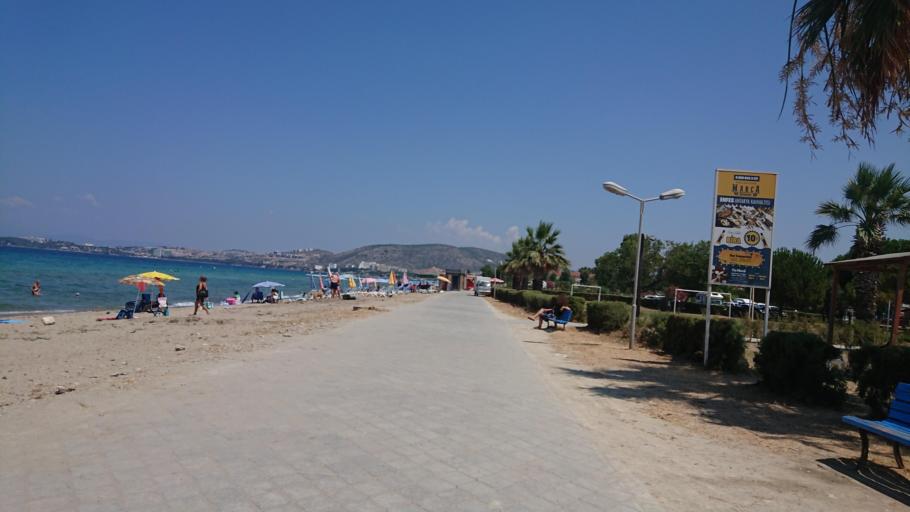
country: TR
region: Aydin
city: Kusadasi
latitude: 37.7964
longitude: 27.2684
